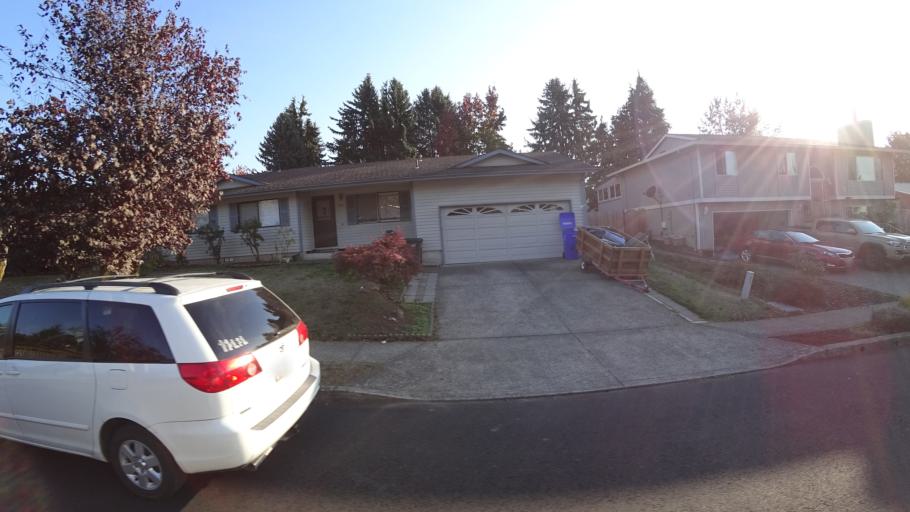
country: US
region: Oregon
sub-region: Multnomah County
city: Gresham
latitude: 45.5085
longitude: -122.4498
